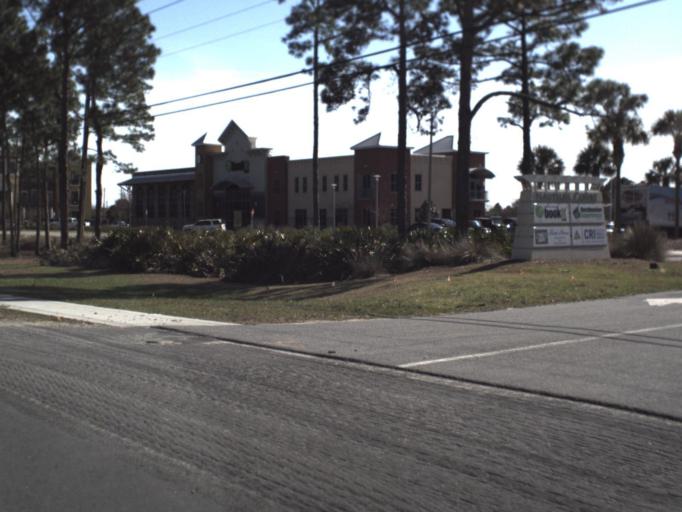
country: US
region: Florida
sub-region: Bay County
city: Panama City Beach
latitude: 30.2120
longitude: -85.8517
